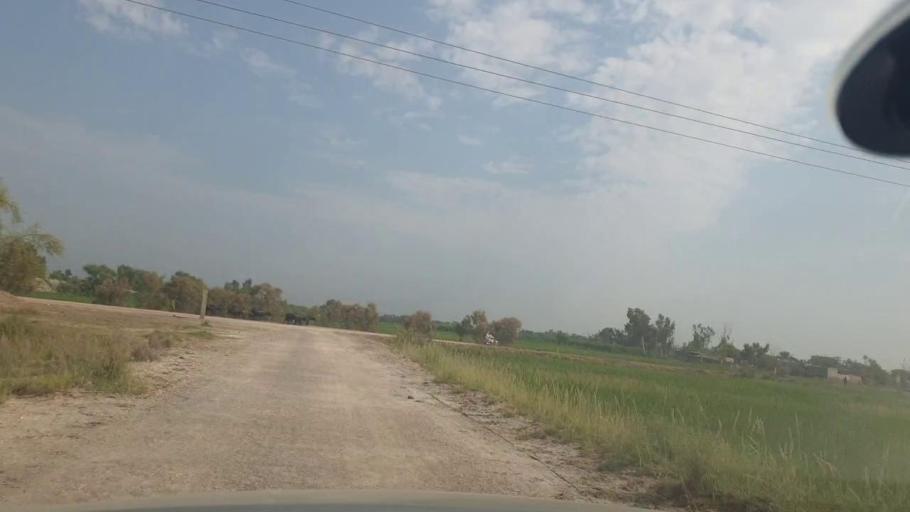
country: PK
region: Balochistan
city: Mehrabpur
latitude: 28.0580
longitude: 68.1243
